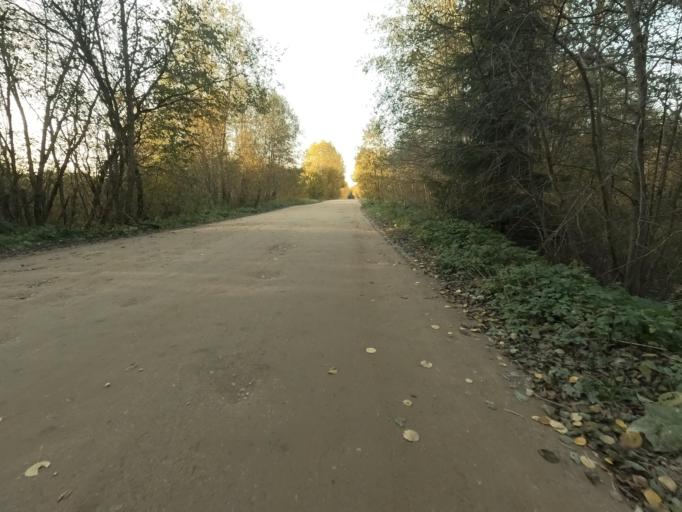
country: RU
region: Leningrad
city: Lyuban'
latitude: 59.0086
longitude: 31.0919
